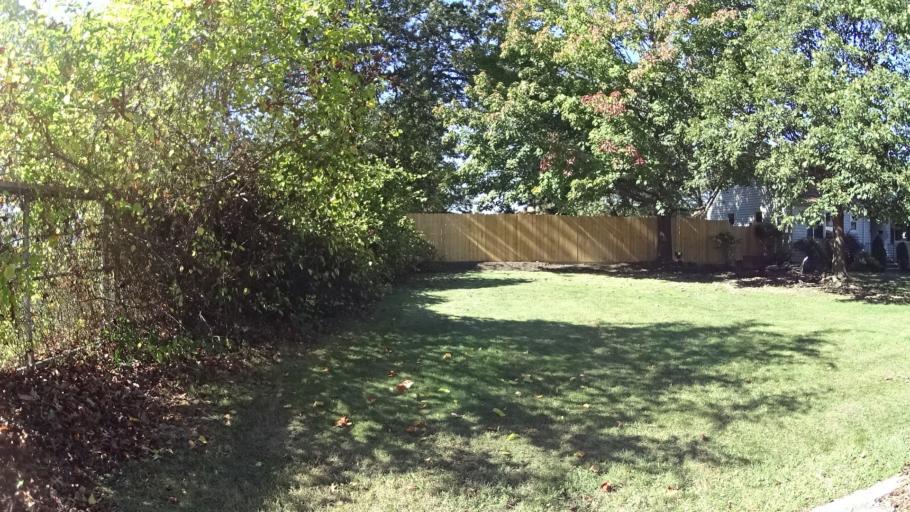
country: US
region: Ohio
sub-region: Lorain County
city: Lorain
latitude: 41.4394
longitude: -82.1806
